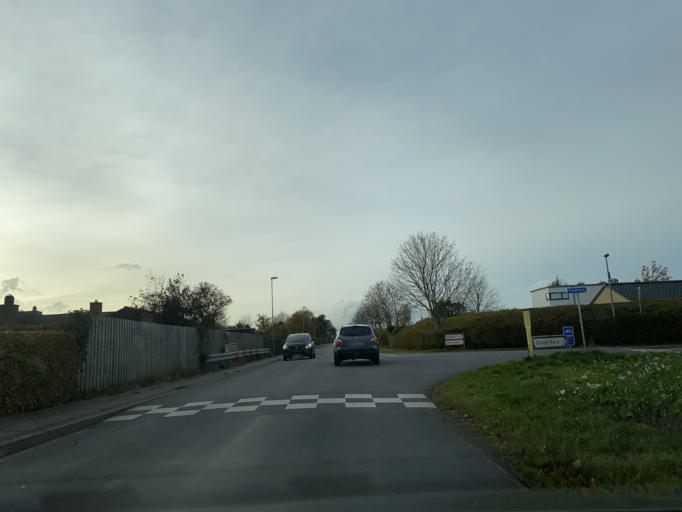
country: DK
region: Central Jutland
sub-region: Skanderborg Kommune
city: Skovby
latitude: 56.1592
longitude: 9.9583
